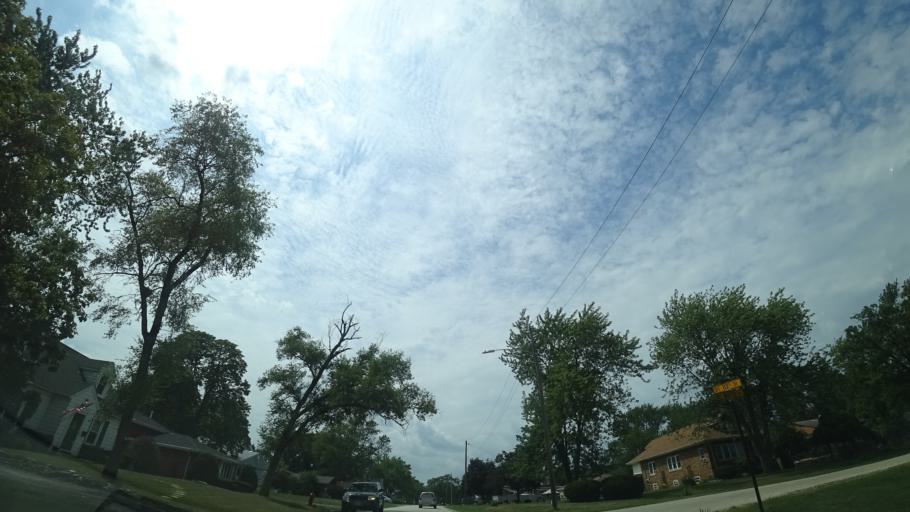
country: US
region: Illinois
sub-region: Cook County
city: Worth
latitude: 41.6863
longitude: -87.7933
